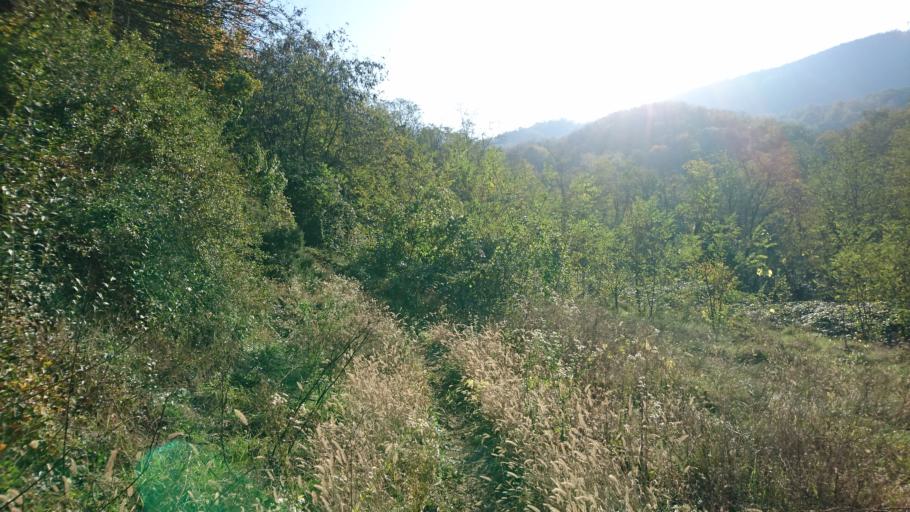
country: IT
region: Veneto
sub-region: Provincia di Padova
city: Fontanafredda
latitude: 45.3237
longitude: 11.6843
